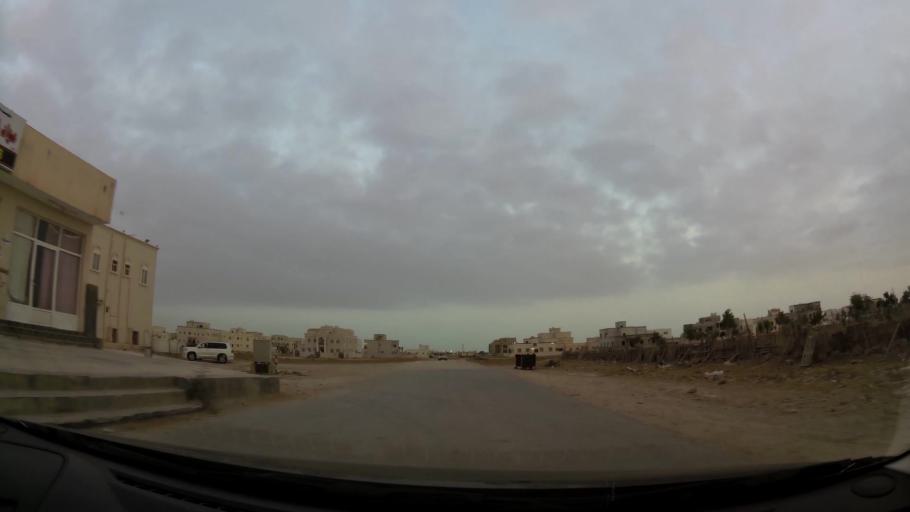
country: OM
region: Zufar
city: Salalah
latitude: 17.0398
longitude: 54.0335
